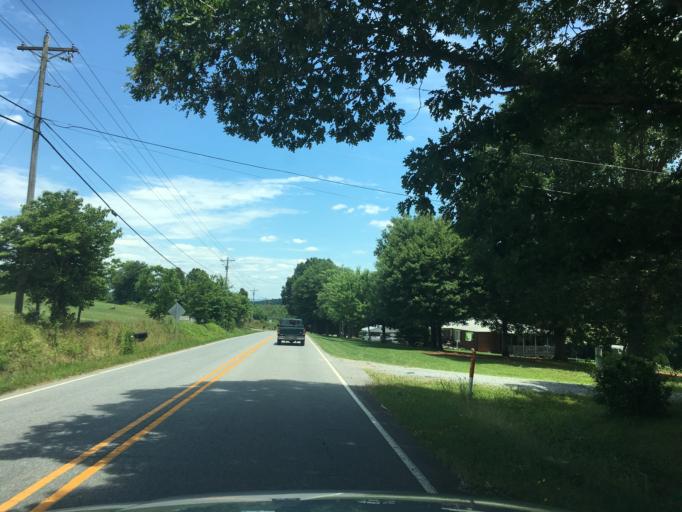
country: US
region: North Carolina
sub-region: Burke County
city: Glen Alpine
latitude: 35.6895
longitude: -81.7675
